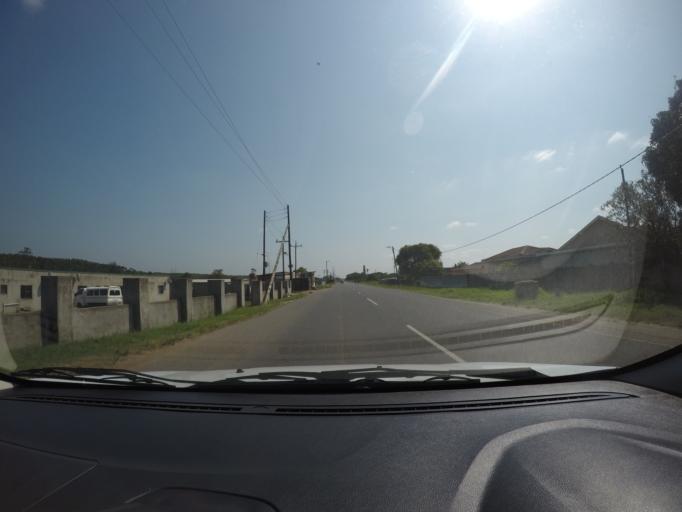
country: ZA
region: KwaZulu-Natal
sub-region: uThungulu District Municipality
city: eSikhawini
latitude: -28.8863
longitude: 31.8844
